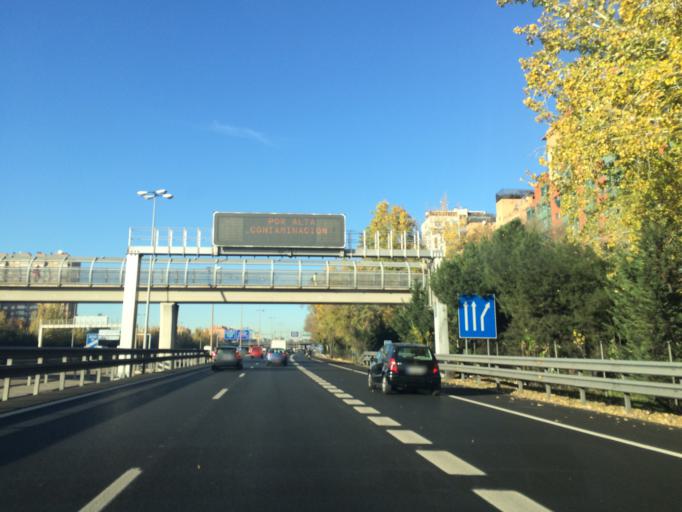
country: ES
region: Madrid
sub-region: Provincia de Madrid
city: Ciudad Lineal
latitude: 40.4486
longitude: -3.6618
